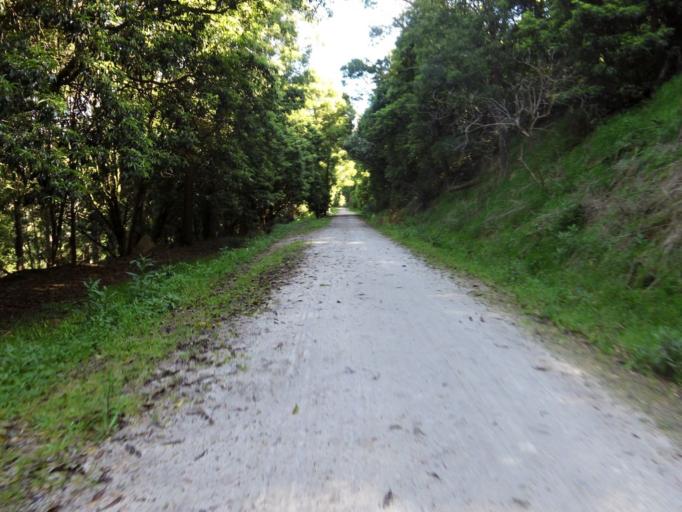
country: AU
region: Victoria
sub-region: Latrobe
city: Morwell
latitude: -38.6795
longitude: 146.1589
